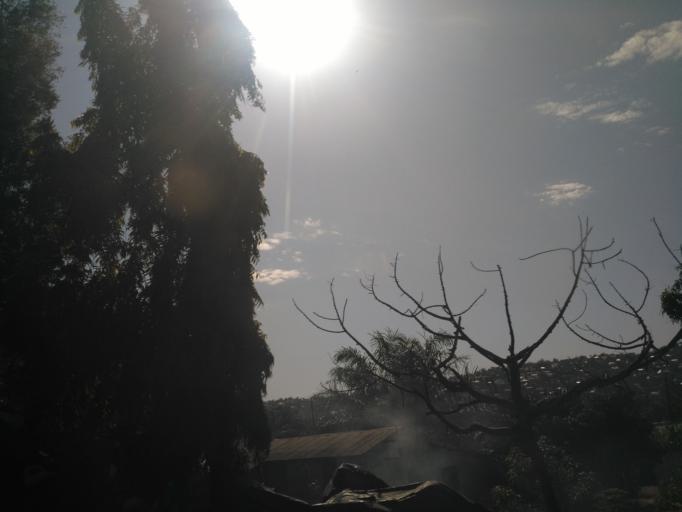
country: TZ
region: Mwanza
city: Mwanza
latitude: -2.4971
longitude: 32.8977
